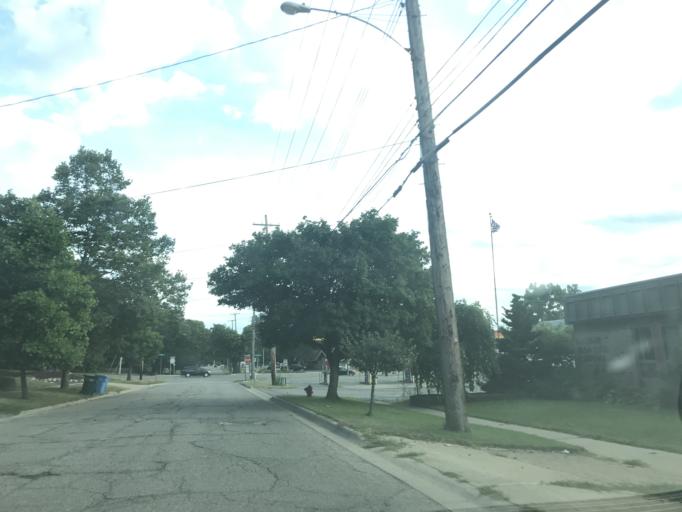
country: US
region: Michigan
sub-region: Ingham County
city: Lansing
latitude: 42.7443
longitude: -84.5481
